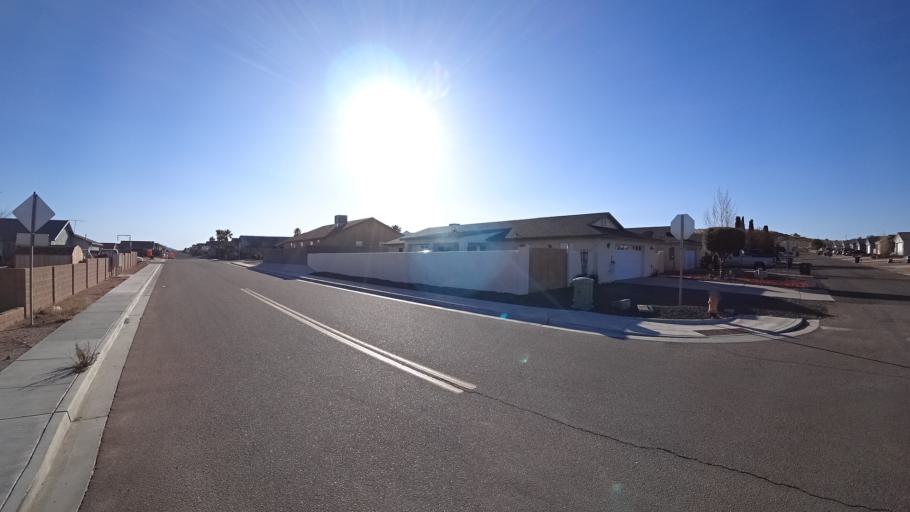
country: US
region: Arizona
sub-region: Mohave County
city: Kingman
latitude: 35.2140
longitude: -114.0092
